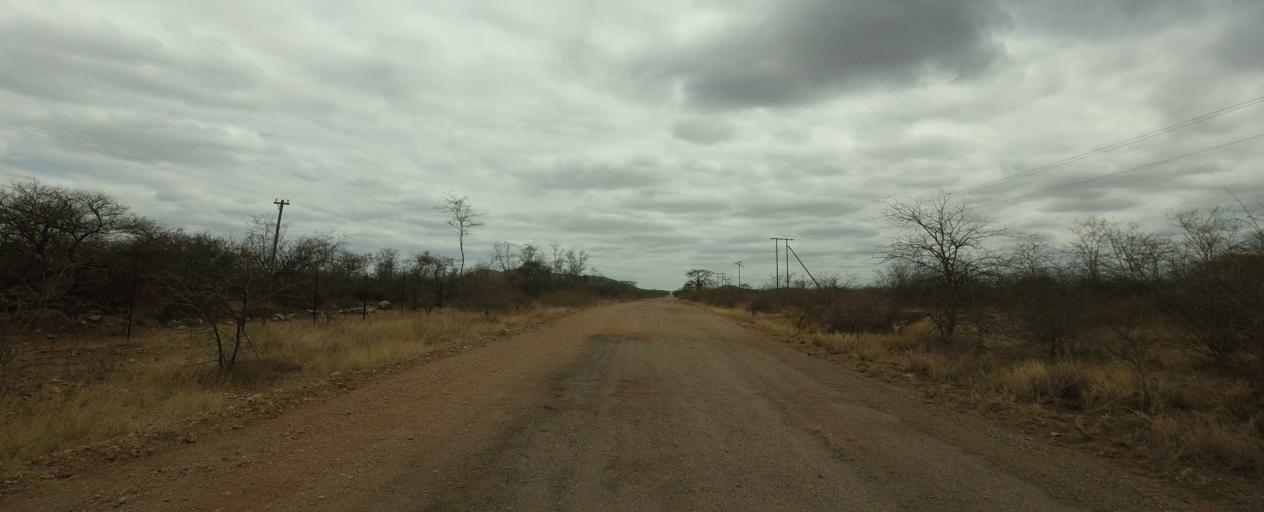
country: BW
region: Central
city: Mogapi
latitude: -22.7892
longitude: 28.3044
